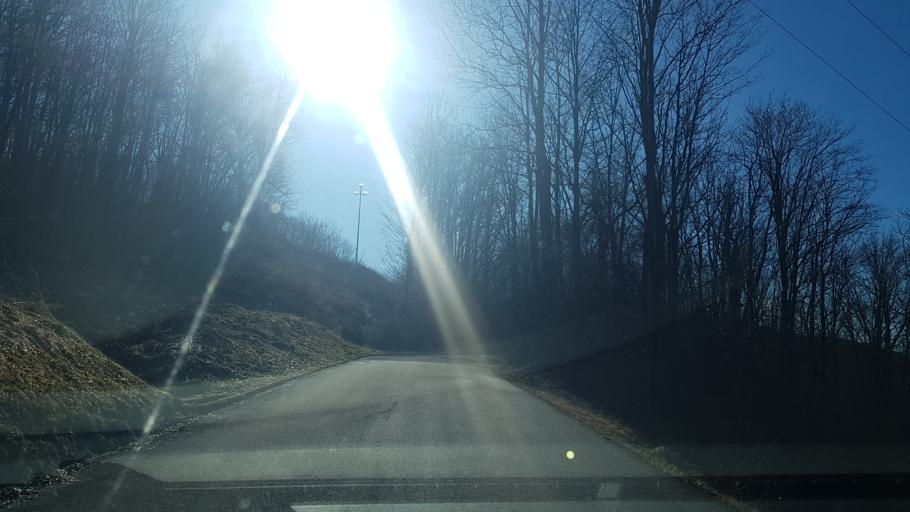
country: IT
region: Friuli Venezia Giulia
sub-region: Provincia di Udine
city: Isola
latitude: 46.2635
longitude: 13.1987
